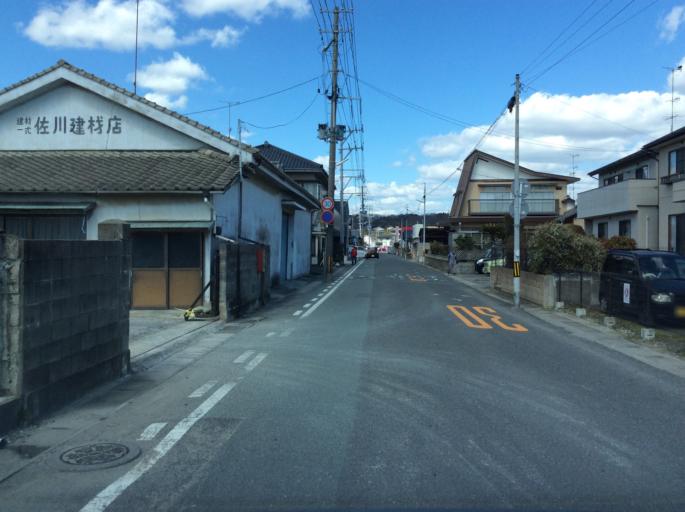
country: JP
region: Fukushima
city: Iwaki
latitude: 36.9558
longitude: 140.9050
